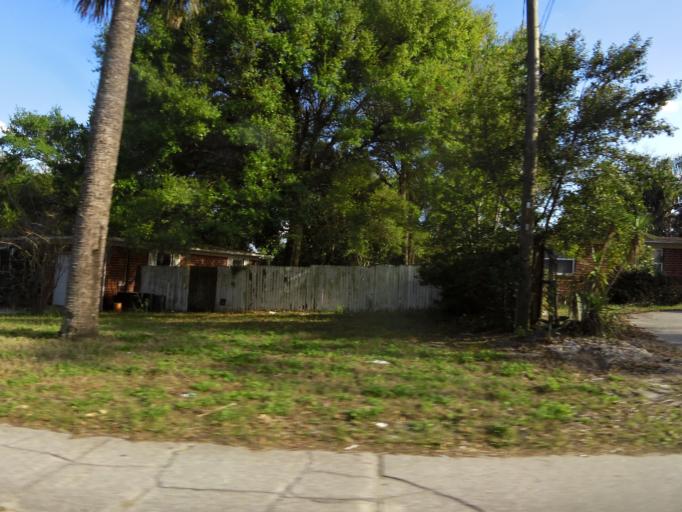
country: US
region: Florida
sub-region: Duval County
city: Jacksonville
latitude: 30.3488
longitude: -81.5973
